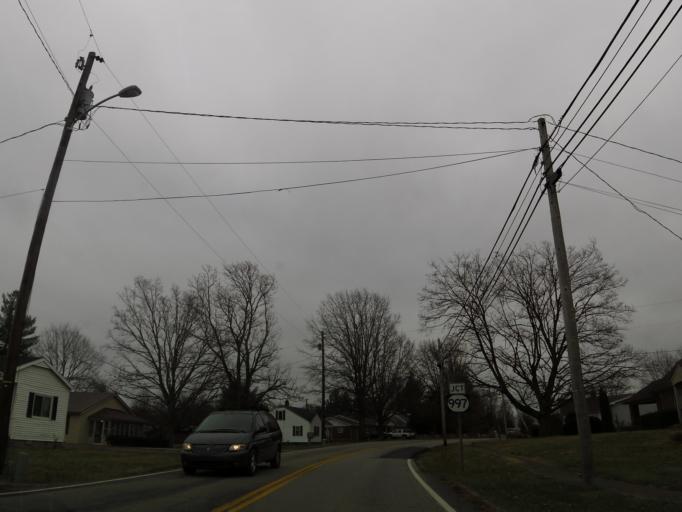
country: US
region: Kentucky
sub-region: Trimble County
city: Providence
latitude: 38.5244
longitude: -85.2090
